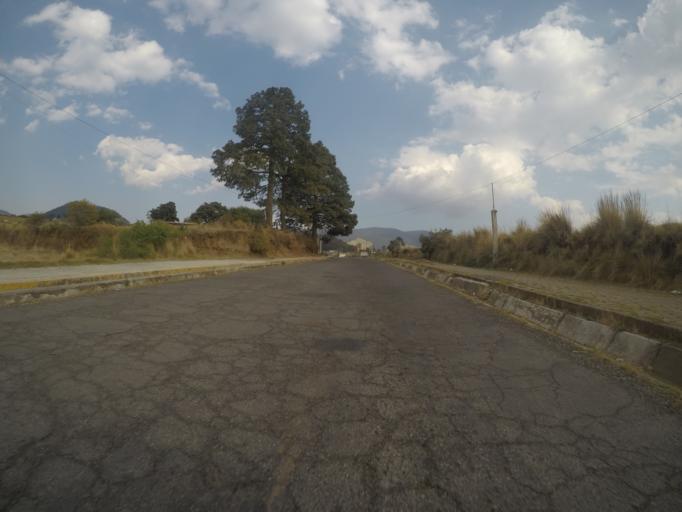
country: MX
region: Mexico
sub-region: Xalatlaco
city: El Aguila (La Mesa)
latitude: 19.1587
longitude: -99.4032
